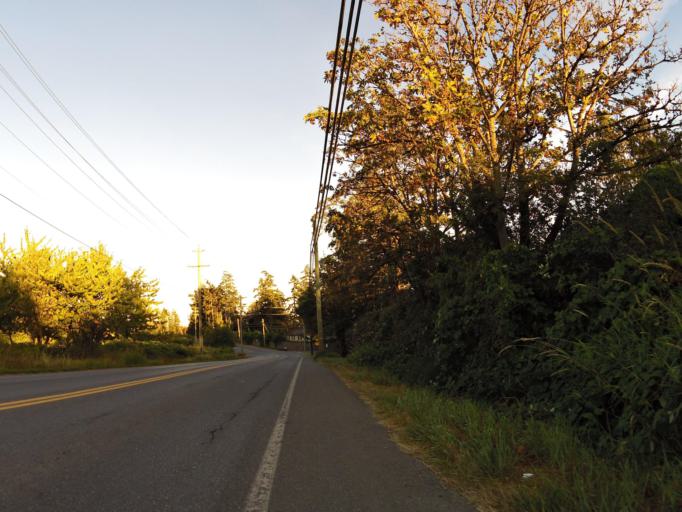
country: CA
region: British Columbia
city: North Cowichan
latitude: 48.8623
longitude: -123.5167
